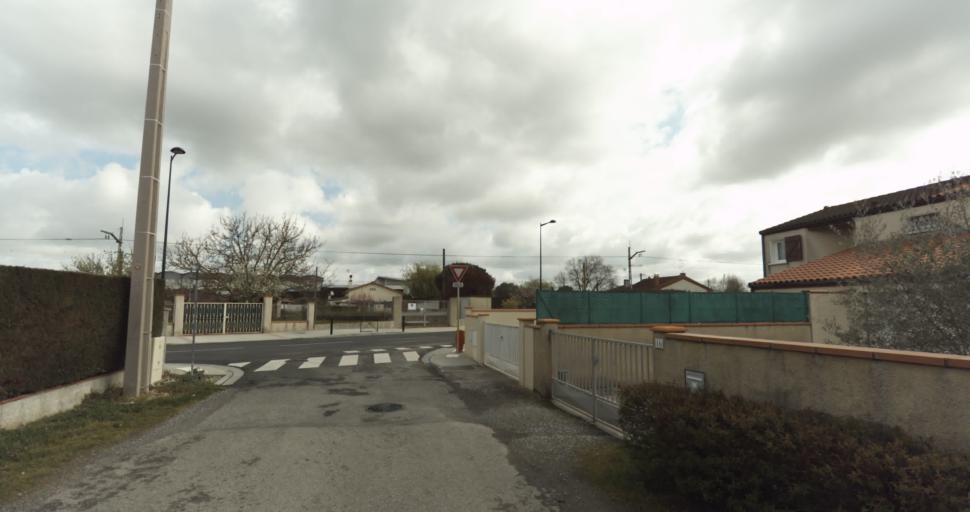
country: FR
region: Midi-Pyrenees
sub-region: Departement de la Haute-Garonne
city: Auterive
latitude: 43.3557
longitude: 1.4622
